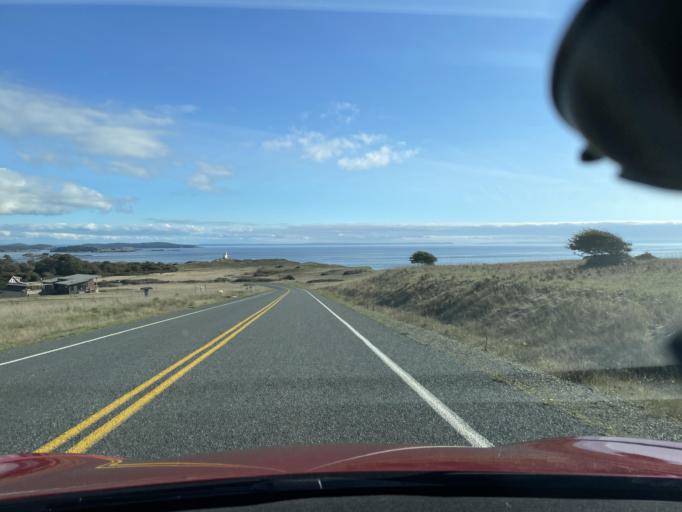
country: US
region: Washington
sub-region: San Juan County
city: Friday Harbor
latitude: 48.4540
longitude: -122.9705
